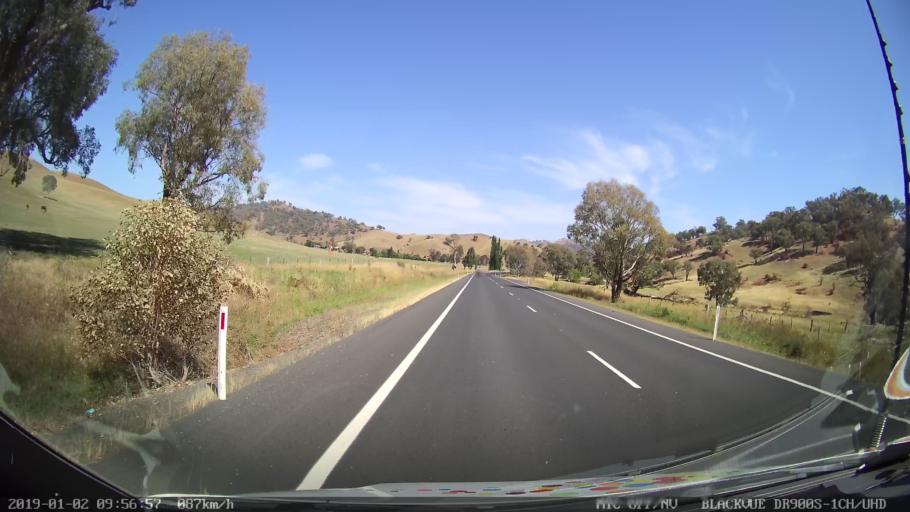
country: AU
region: New South Wales
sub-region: Tumut Shire
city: Tumut
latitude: -35.2108
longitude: 148.1707
